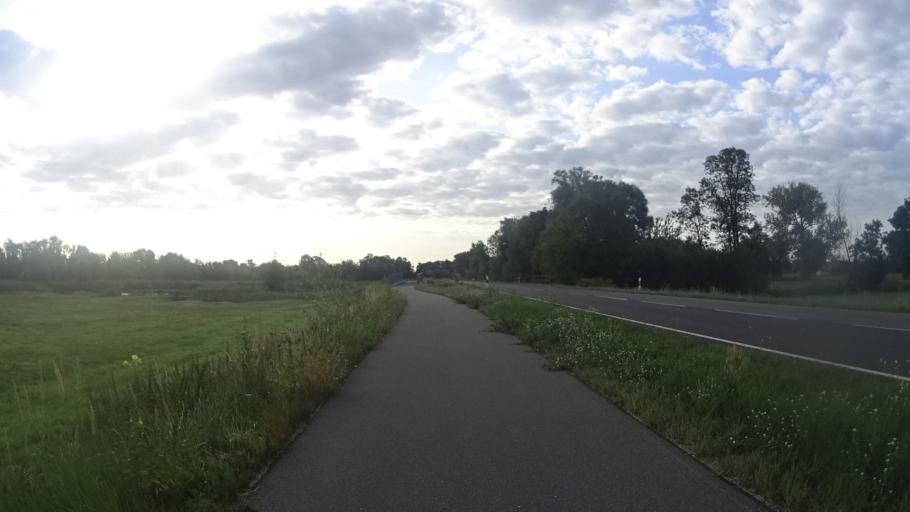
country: DE
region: Brandenburg
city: Premnitz
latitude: 52.5011
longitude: 12.4526
